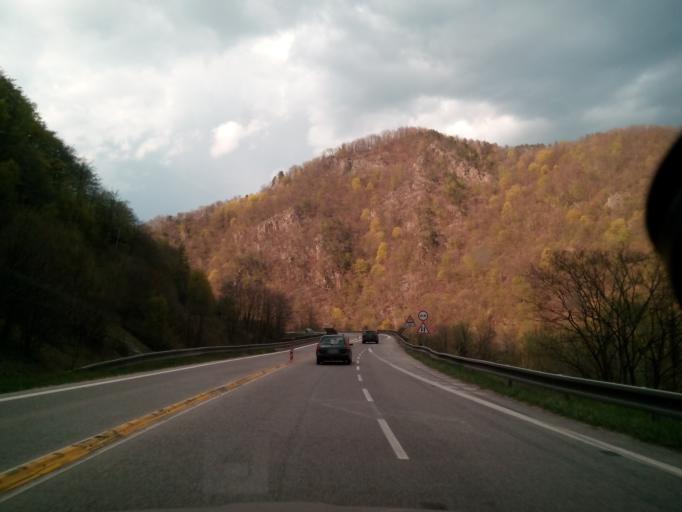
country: SK
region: Zilinsky
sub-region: Okres Zilina
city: Vrutky
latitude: 49.1571
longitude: 18.8847
